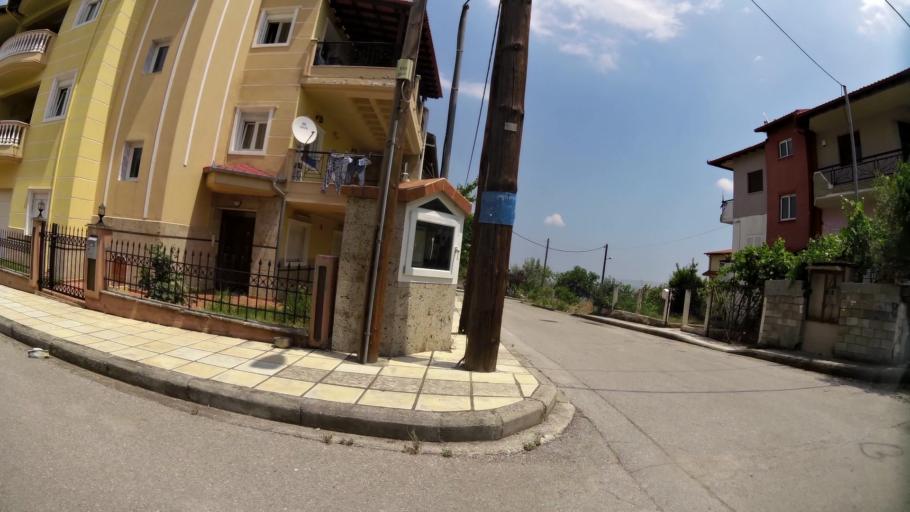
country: GR
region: Central Macedonia
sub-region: Nomos Imathias
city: Veroia
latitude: 40.5119
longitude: 22.1811
